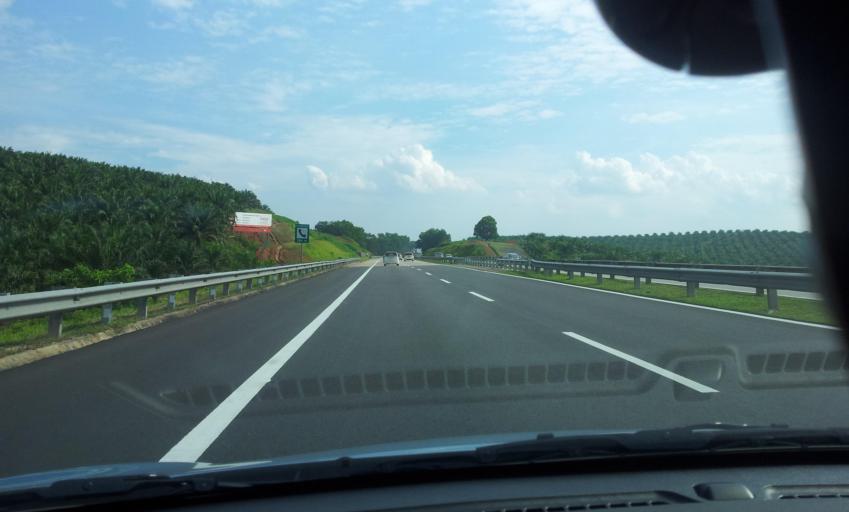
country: MY
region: Pahang
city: Temerluh
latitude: 3.5629
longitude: 102.5535
